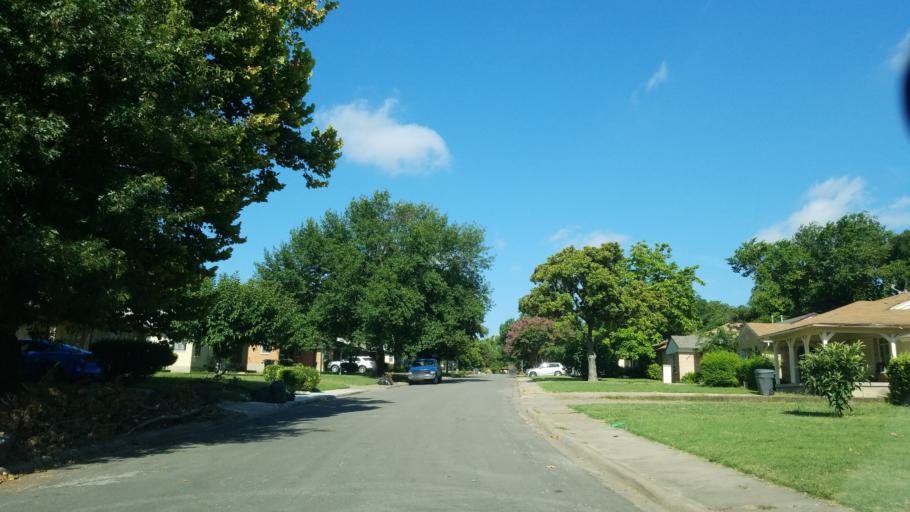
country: US
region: Texas
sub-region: Dallas County
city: Dallas
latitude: 32.7136
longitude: -96.8003
